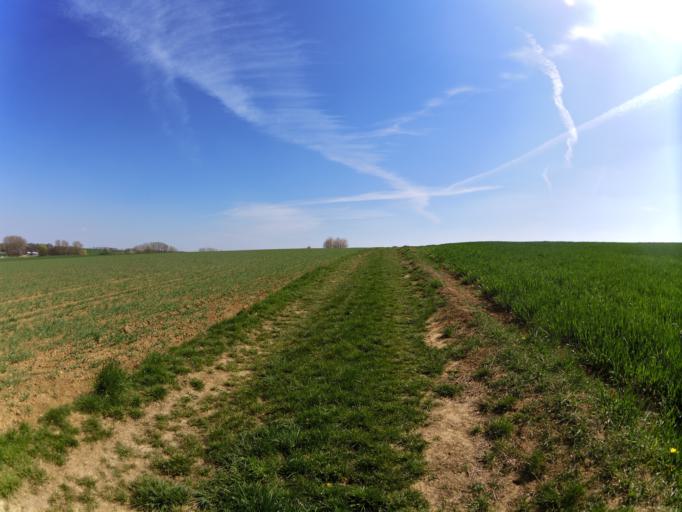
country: DE
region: Bavaria
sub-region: Regierungsbezirk Unterfranken
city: Kurnach
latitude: 49.8636
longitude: 10.0163
